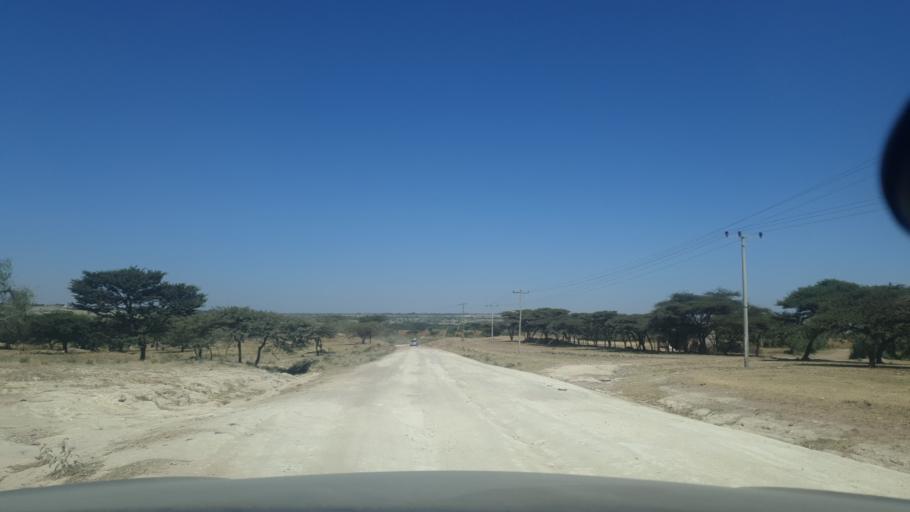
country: ET
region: Oromiya
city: Shashemene
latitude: 7.5057
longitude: 38.6894
